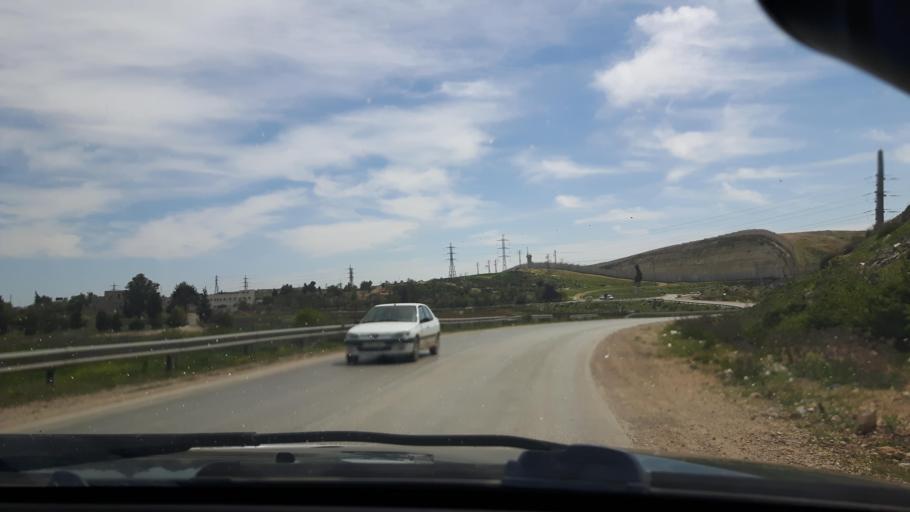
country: PS
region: West Bank
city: Qalandiya
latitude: 31.8637
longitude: 35.2028
